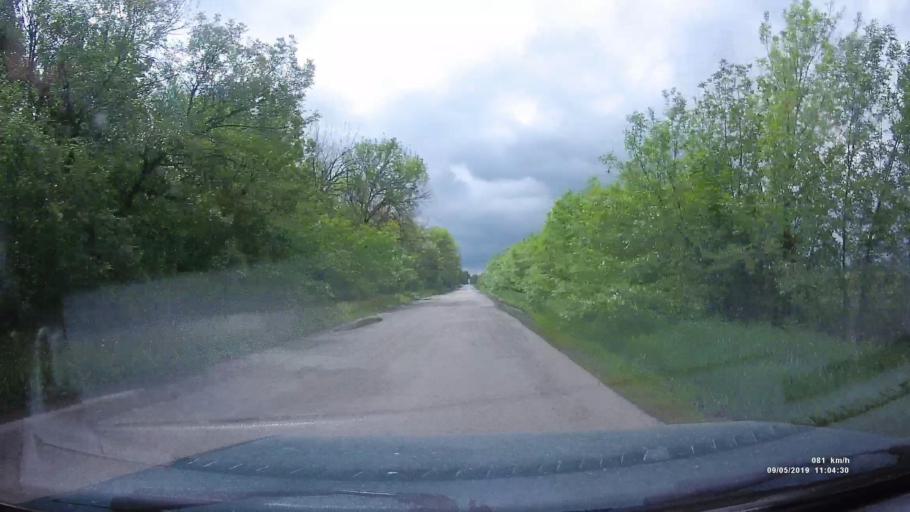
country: RU
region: Krasnodarskiy
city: Kanelovskaya
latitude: 46.8163
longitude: 39.2099
